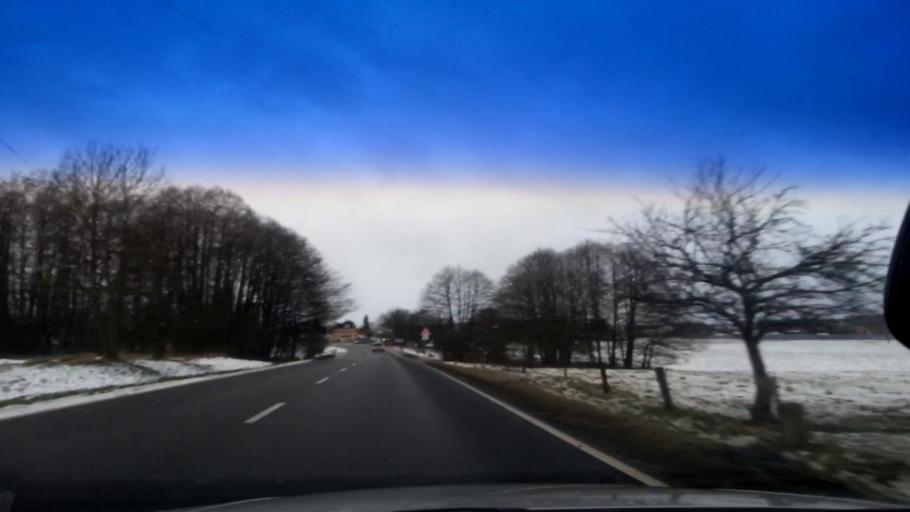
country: CZ
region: Karlovarsky
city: Hazlov
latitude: 50.1525
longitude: 12.2845
